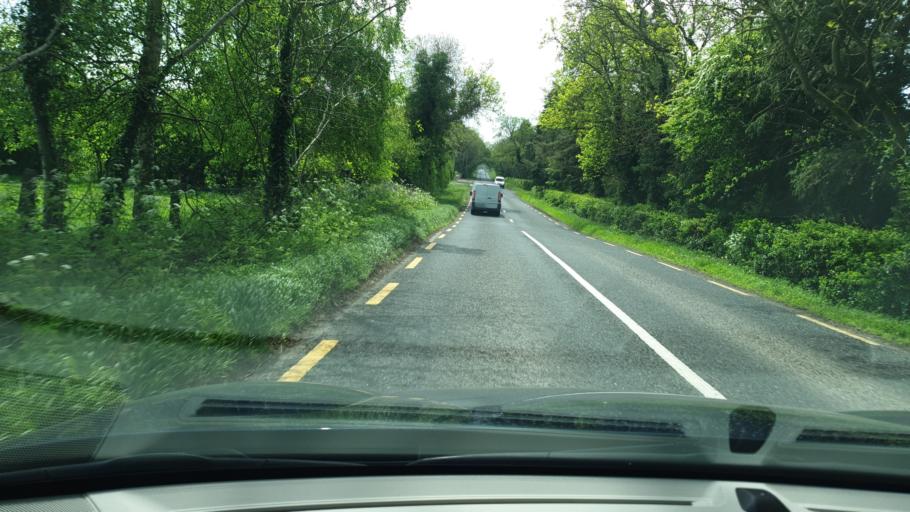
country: IE
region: Leinster
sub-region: An Mhi
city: Navan
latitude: 53.7468
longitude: -6.7179
